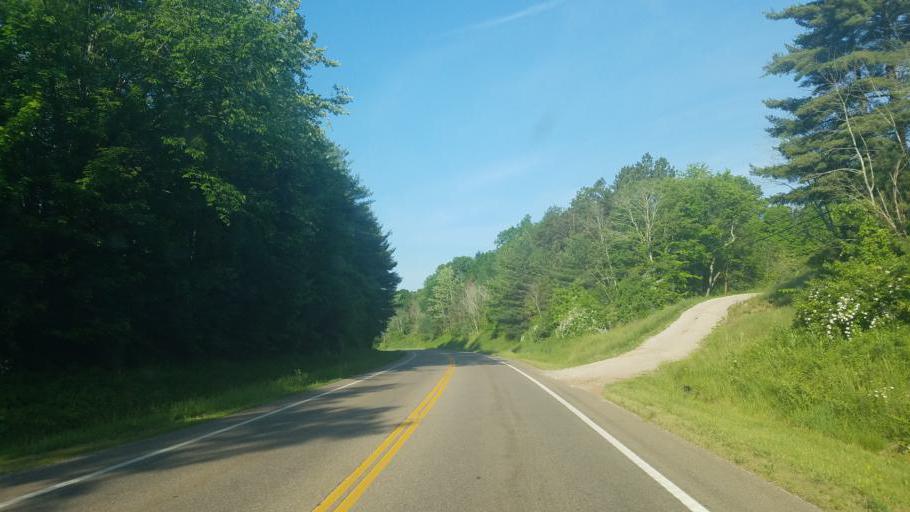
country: US
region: West Virginia
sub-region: Mason County
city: New Haven
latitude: 39.1166
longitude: -81.9134
